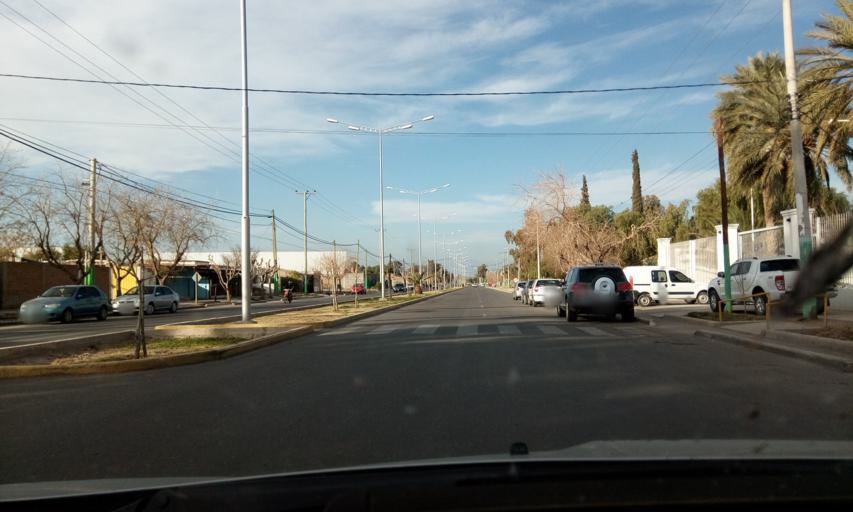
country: AR
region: San Juan
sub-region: Departamento de Rivadavia
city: Rivadavia
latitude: -31.5242
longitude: -68.6242
